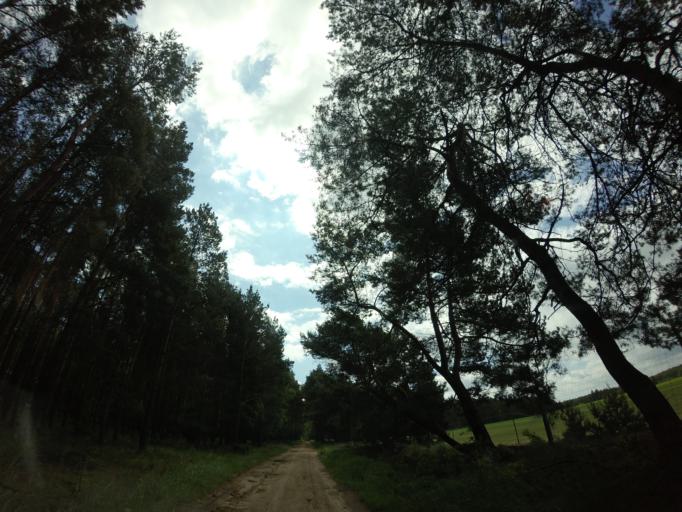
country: PL
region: West Pomeranian Voivodeship
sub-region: Powiat choszczenski
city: Drawno
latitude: 53.1803
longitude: 15.8707
